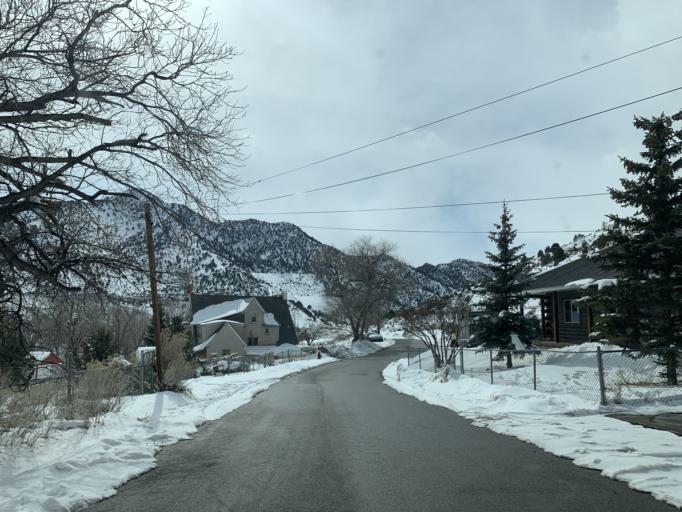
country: US
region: Utah
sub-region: Utah County
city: Genola
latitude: 39.9572
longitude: -112.1229
